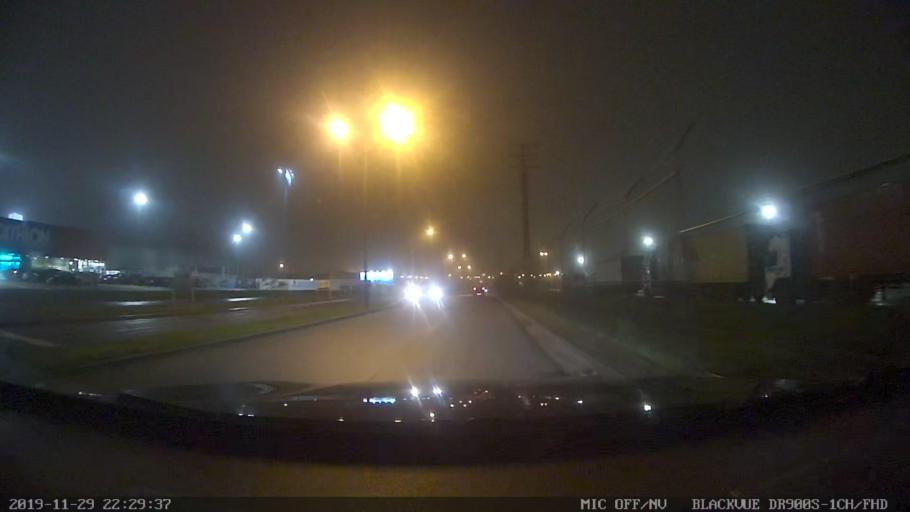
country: PT
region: Porto
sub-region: Matosinhos
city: Santa Cruz do Bispo
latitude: 41.2173
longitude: -8.6838
